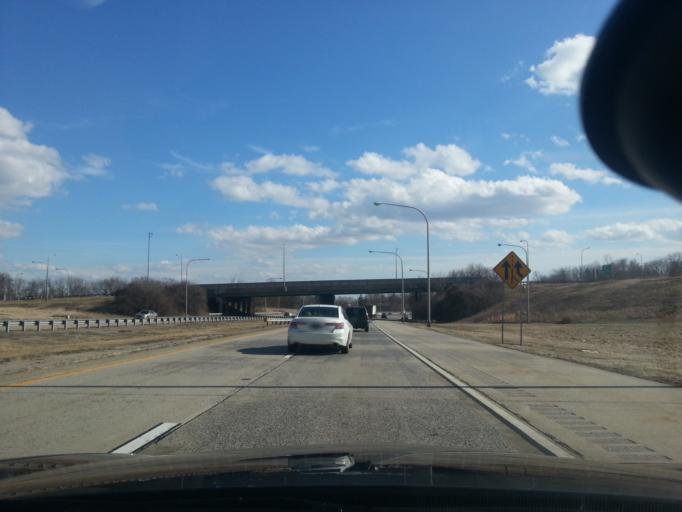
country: US
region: Delaware
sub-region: New Castle County
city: Claymont
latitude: 39.8071
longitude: -75.4526
